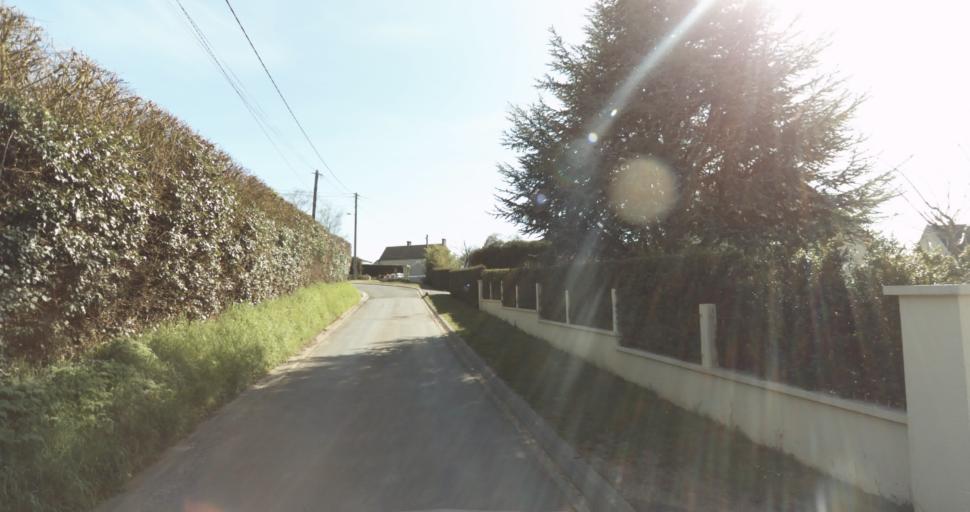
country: FR
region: Lower Normandy
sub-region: Departement du Calvados
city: Saint-Pierre-sur-Dives
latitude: 49.0067
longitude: -0.0458
